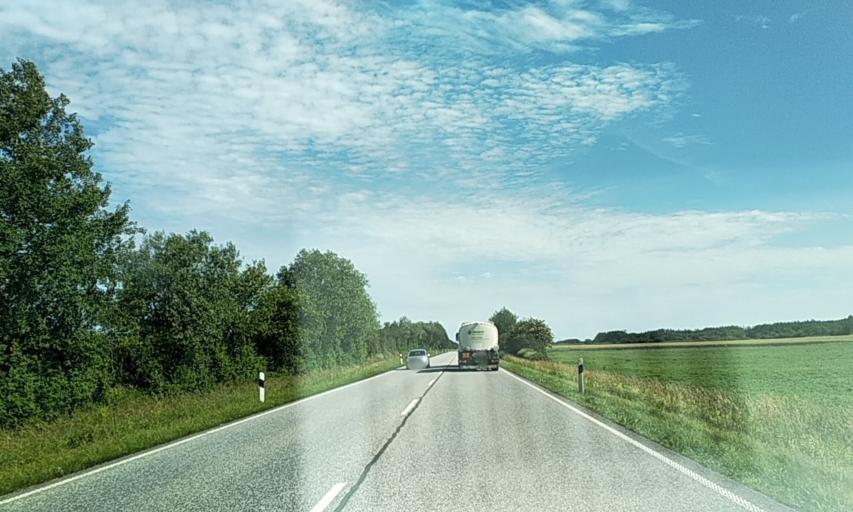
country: DE
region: Schleswig-Holstein
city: Kropp
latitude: 54.4244
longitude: 9.5310
